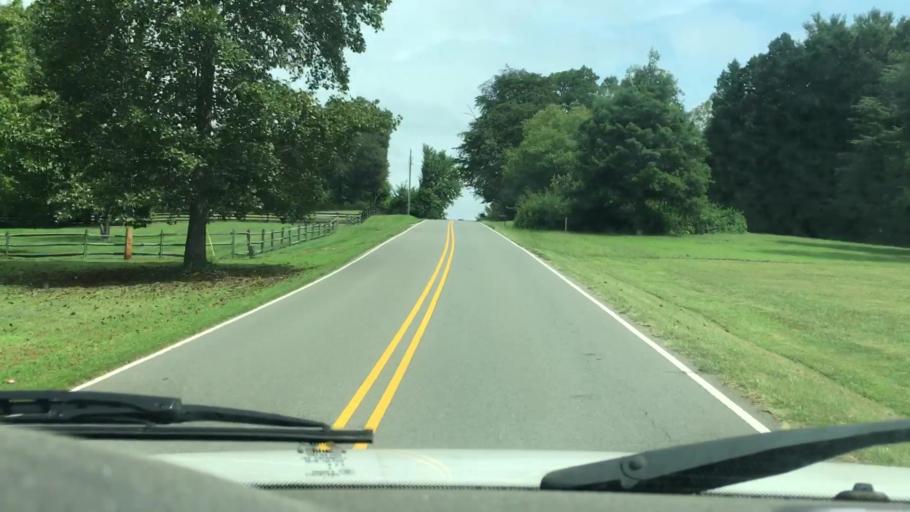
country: US
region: North Carolina
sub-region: Gaston County
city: Davidson
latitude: 35.4994
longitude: -80.8165
